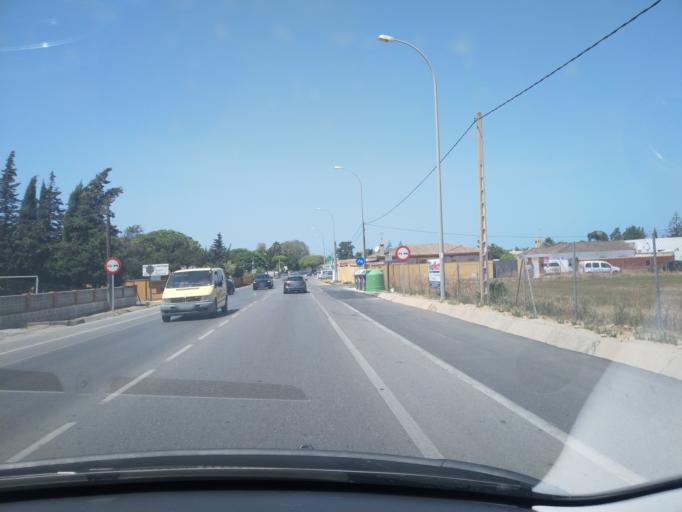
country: ES
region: Andalusia
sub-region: Provincia de Cadiz
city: Chiclana de la Frontera
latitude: 36.3941
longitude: -6.1518
